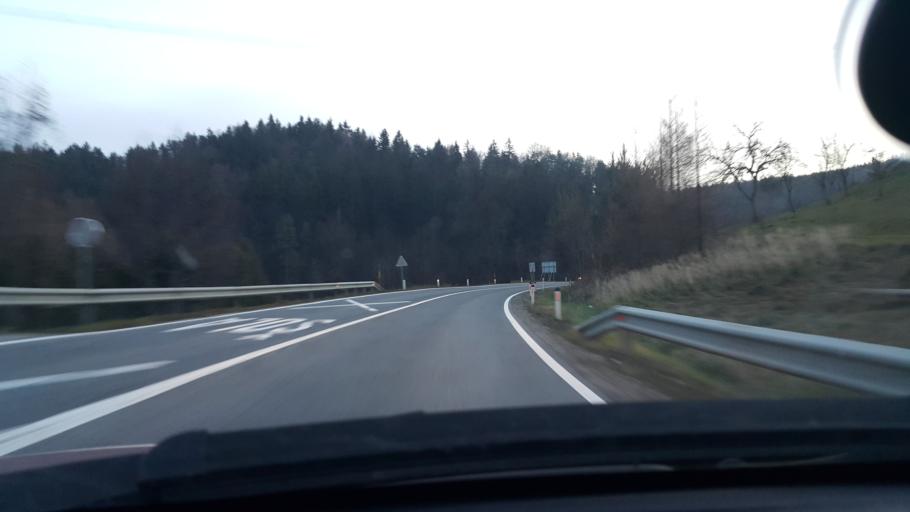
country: SI
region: Dobrna
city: Dobrna
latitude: 46.3406
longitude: 15.1726
